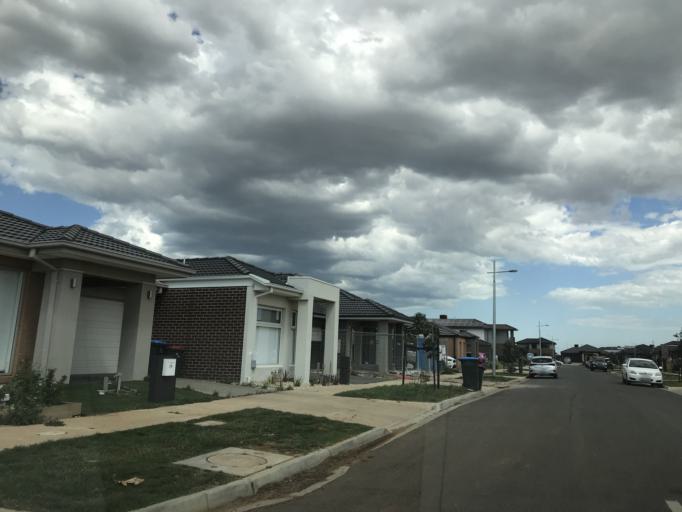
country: AU
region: Victoria
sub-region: Wyndham
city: Truganina
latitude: -37.8184
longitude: 144.7153
